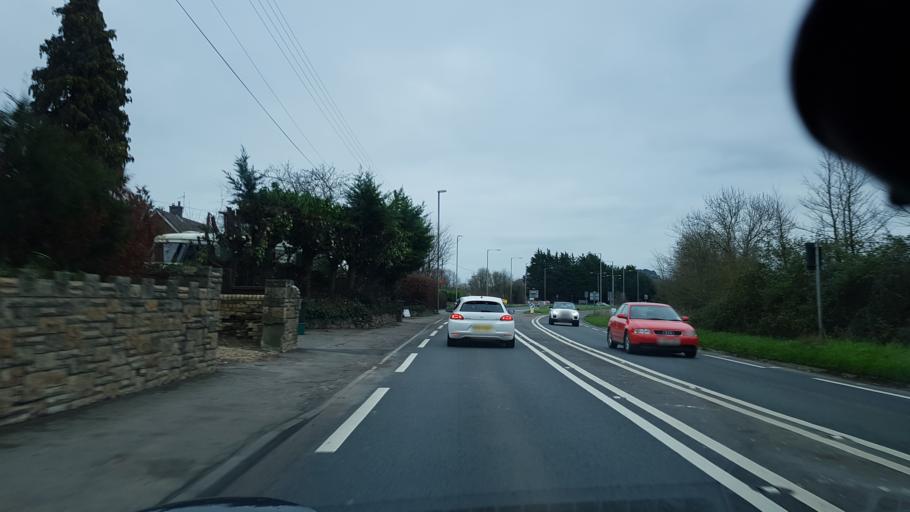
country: GB
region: England
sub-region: Somerset
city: Creech Saint Michael
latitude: 51.0111
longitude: -3.0405
